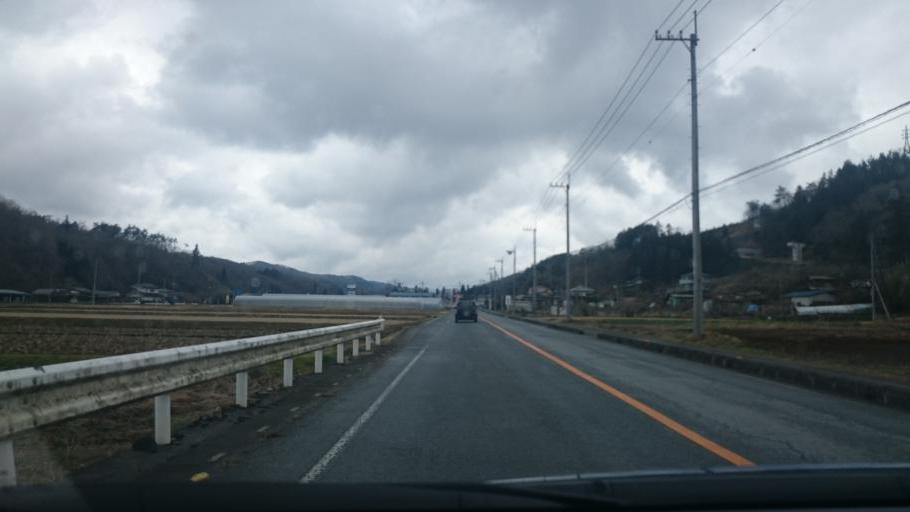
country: JP
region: Saitama
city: Chichibu
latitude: 36.0337
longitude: 139.0770
